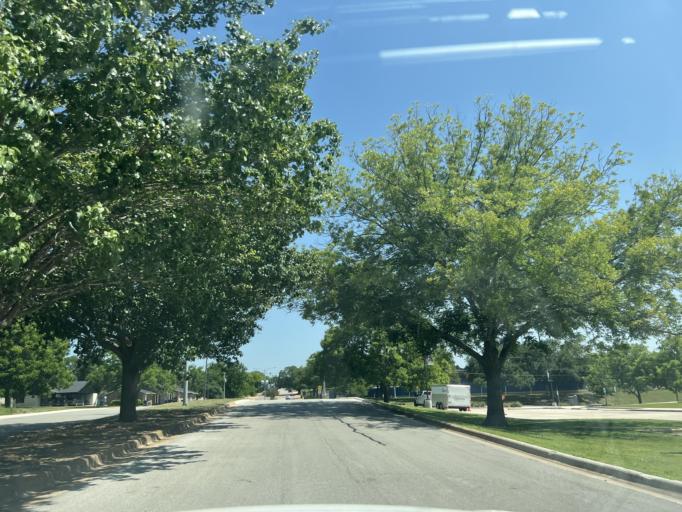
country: US
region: Texas
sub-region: Washington County
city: Brenham
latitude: 30.1634
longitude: -96.4104
